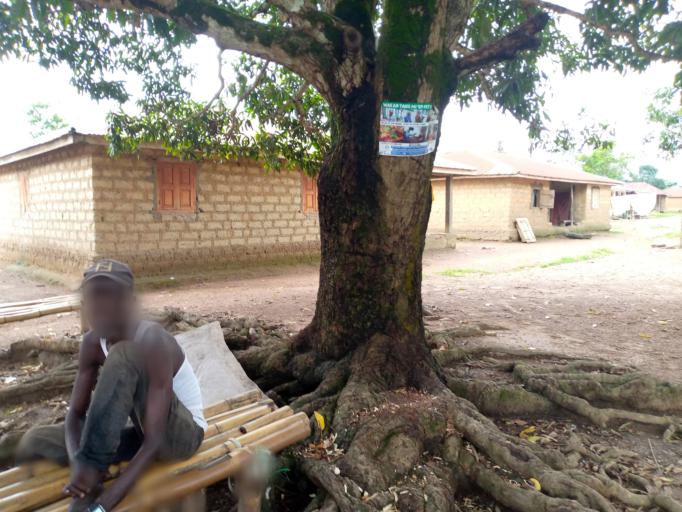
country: SL
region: Northern Province
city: Mange
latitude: 8.9806
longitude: -12.7393
